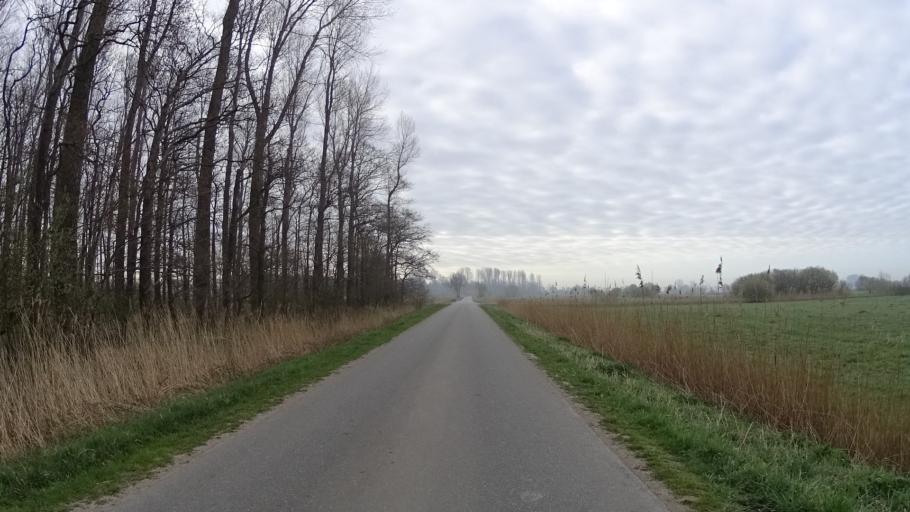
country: DE
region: Lower Saxony
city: Upgant-Schott
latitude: 53.4545
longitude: 7.3291
